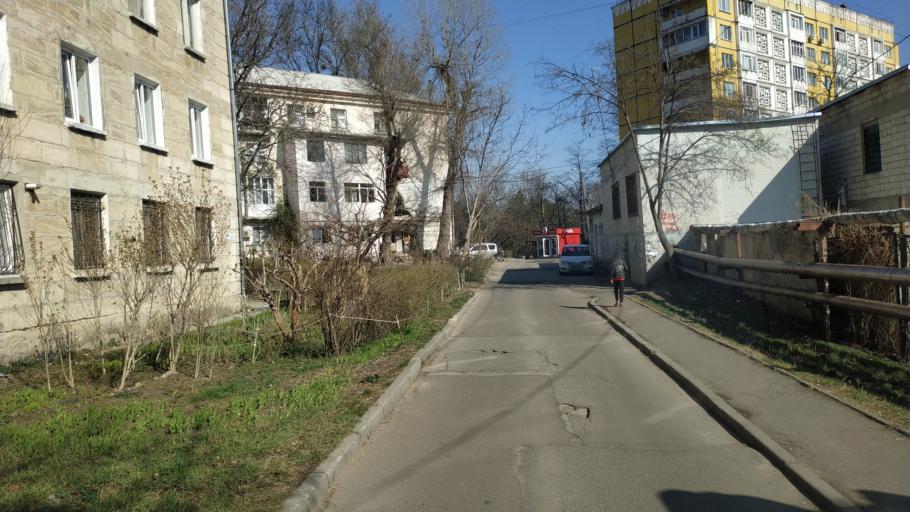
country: MD
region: Chisinau
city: Chisinau
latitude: 47.0215
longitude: 28.8091
